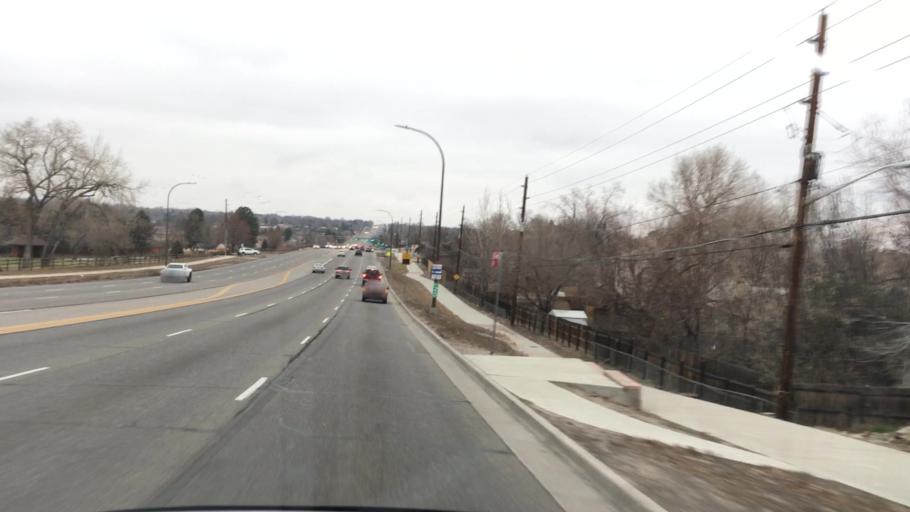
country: US
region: Colorado
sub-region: Jefferson County
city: Arvada
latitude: 39.8307
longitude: -105.0815
